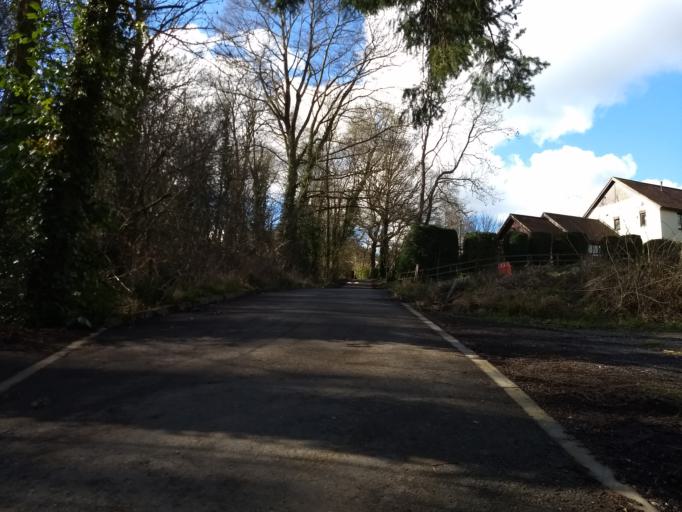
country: GB
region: England
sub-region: Isle of Wight
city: Ryde
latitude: 50.7282
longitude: -1.2188
